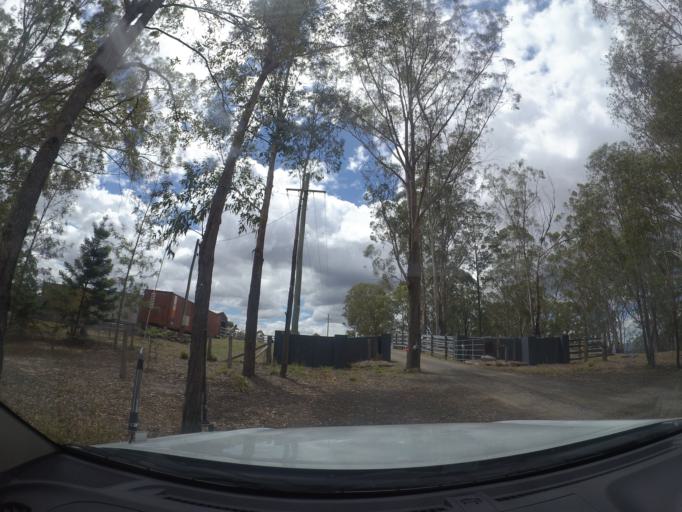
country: AU
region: Queensland
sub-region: Logan
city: Cedar Vale
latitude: -27.9166
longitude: 153.0364
